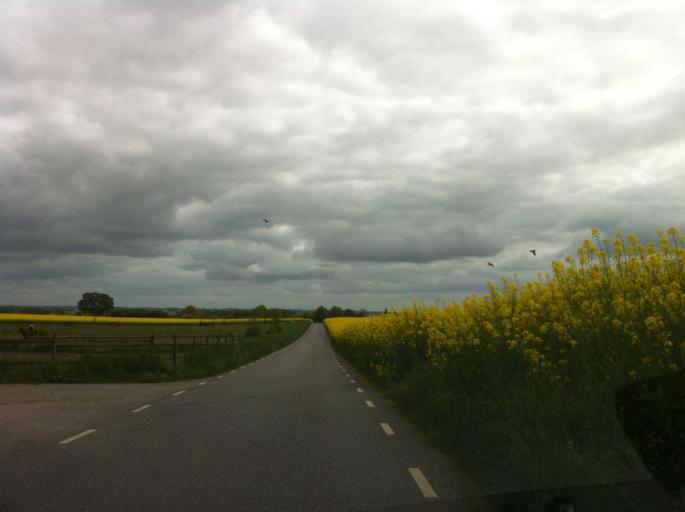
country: SE
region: Skane
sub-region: Svalovs Kommun
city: Teckomatorp
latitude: 55.8415
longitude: 13.0859
